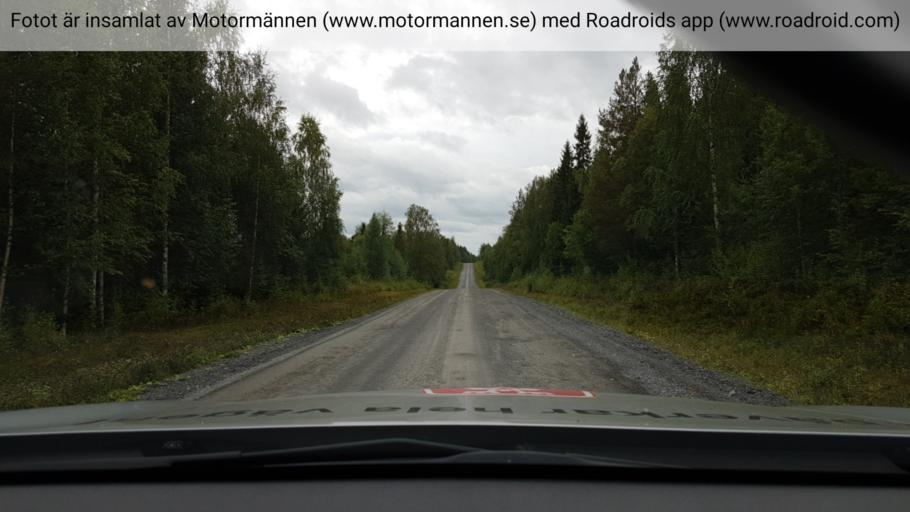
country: SE
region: Vaesterbotten
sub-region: Skelleftea Kommun
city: Forsbacka
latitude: 64.7822
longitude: 20.5140
